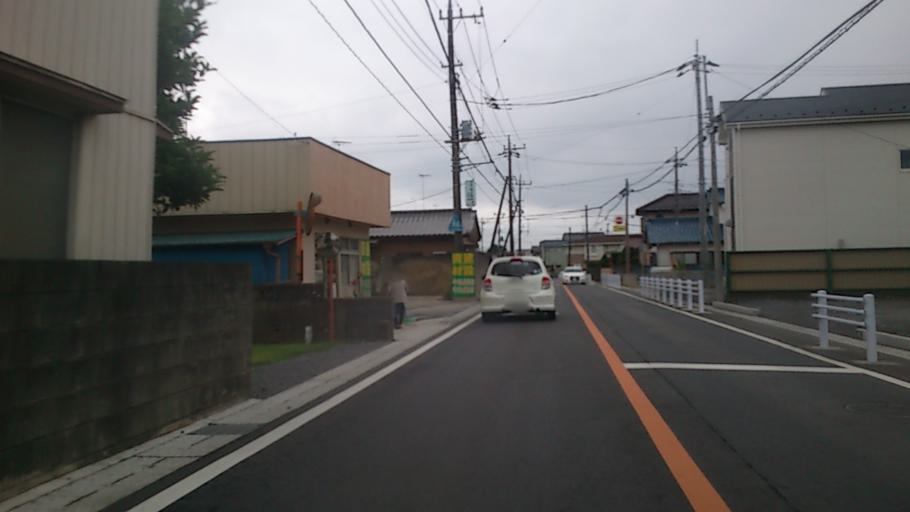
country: JP
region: Ibaraki
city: Ami
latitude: 36.0268
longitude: 140.2197
